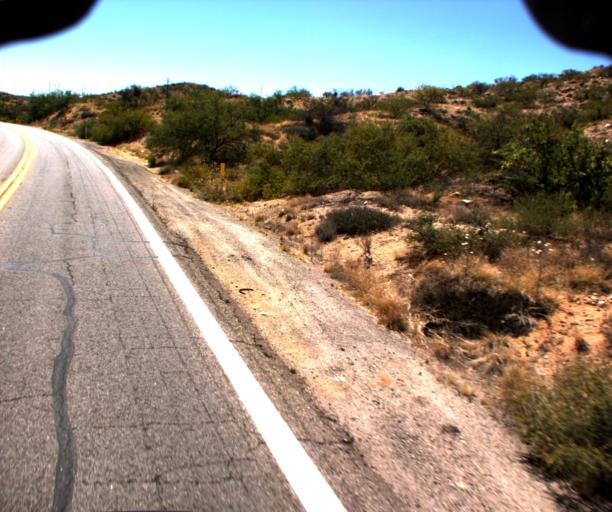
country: US
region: Arizona
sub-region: Pinal County
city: Oracle
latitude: 32.6359
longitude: -110.7325
